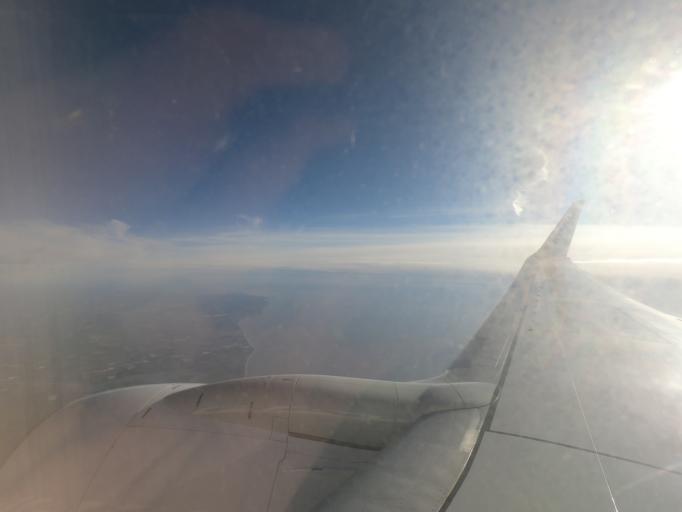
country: GB
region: England
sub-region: Suffolk
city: Aldeburgh
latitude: 52.0064
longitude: 1.5562
